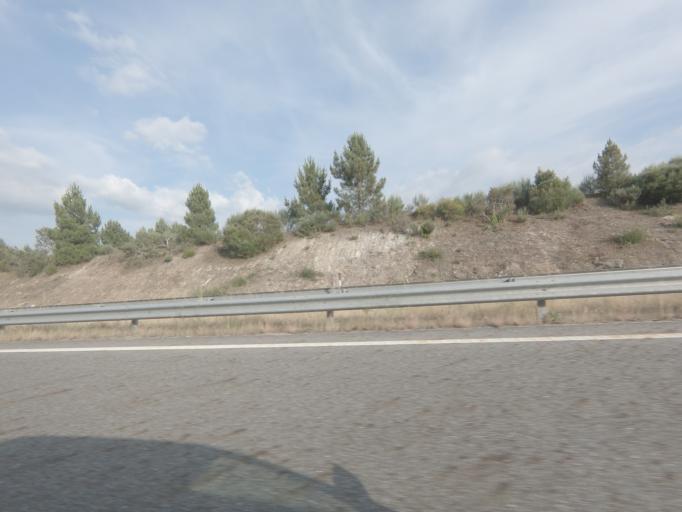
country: PT
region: Vila Real
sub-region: Chaves
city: Chaves
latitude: 41.7613
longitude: -7.5041
